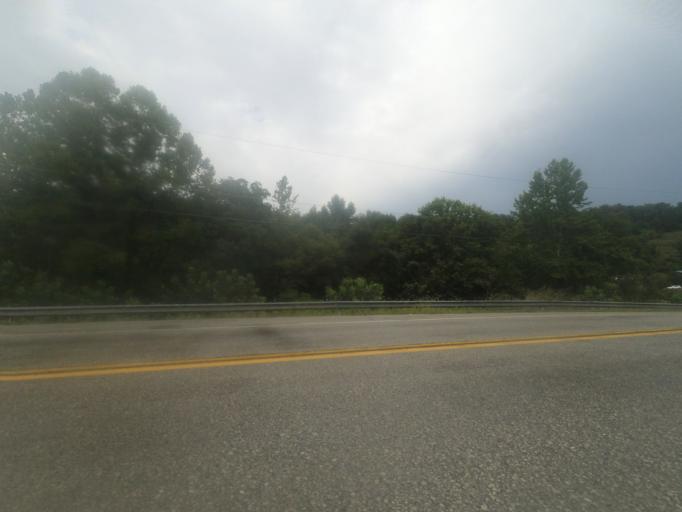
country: US
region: West Virginia
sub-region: Cabell County
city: Huntington
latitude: 38.3894
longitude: -82.3986
